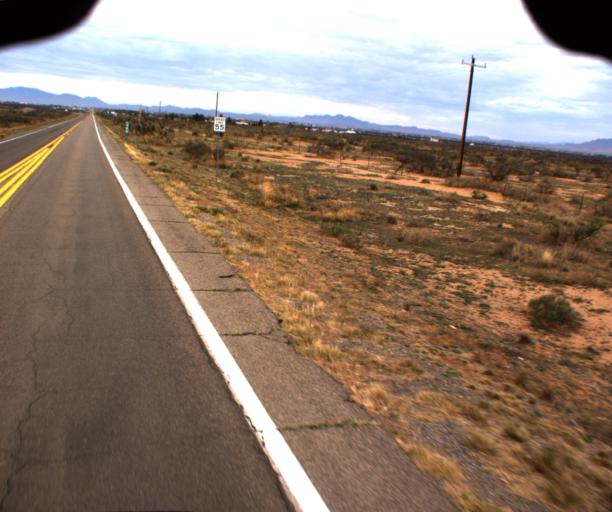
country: US
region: Arizona
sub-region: Cochise County
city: Willcox
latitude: 32.3026
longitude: -109.7978
